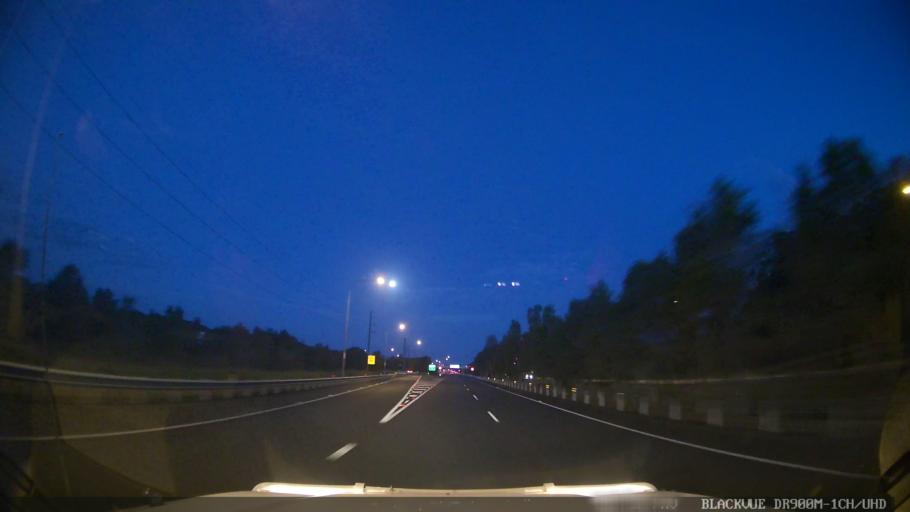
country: AU
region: Queensland
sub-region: Sunshine Coast
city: Buderim
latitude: -26.7109
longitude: 153.0642
